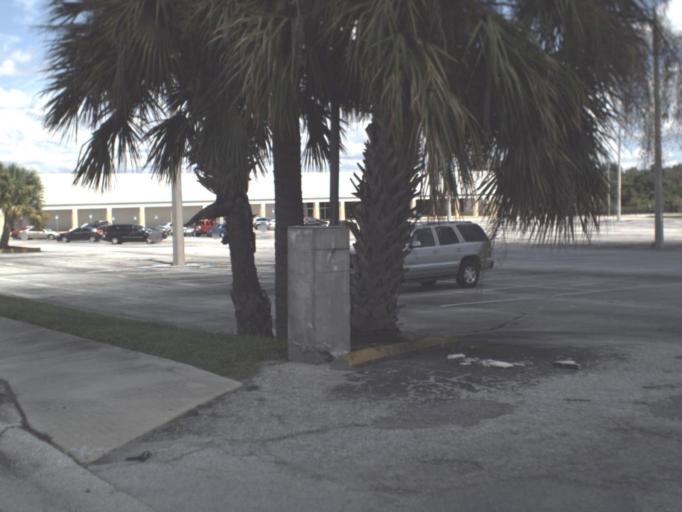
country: US
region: Florida
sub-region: Polk County
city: Lakeland
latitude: 28.0460
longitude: -81.9407
